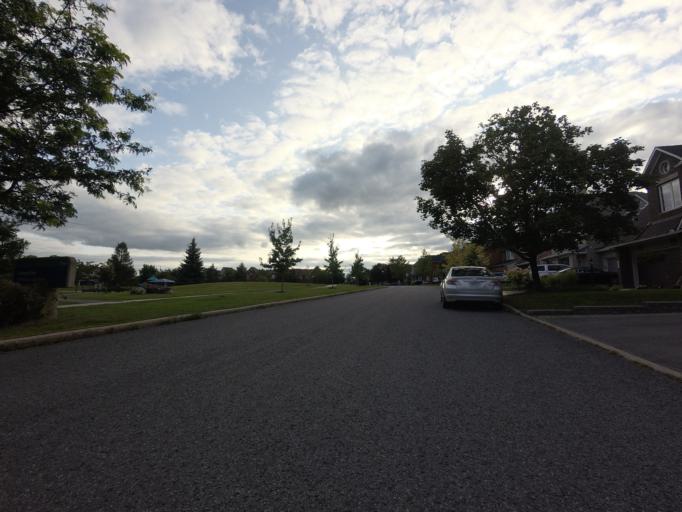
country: CA
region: Ontario
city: Bells Corners
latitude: 45.2769
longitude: -75.7228
